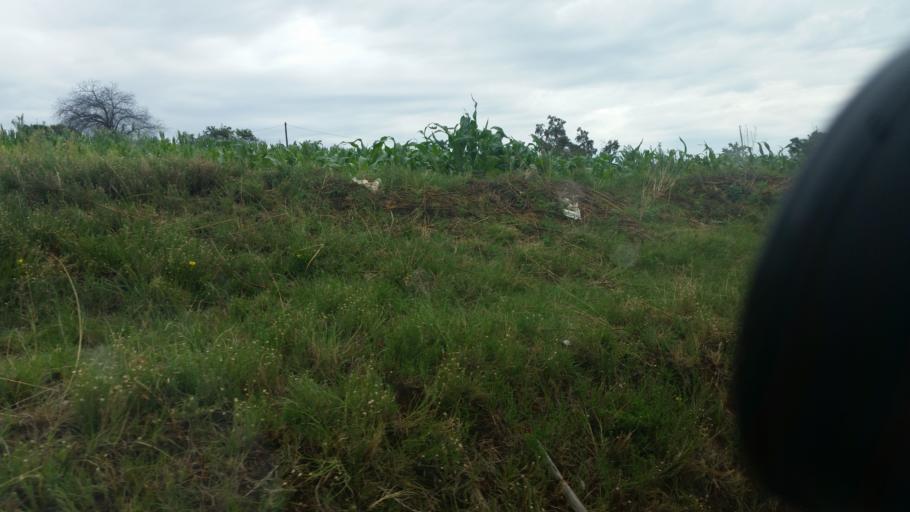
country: LS
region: Berea
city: Teyateyaneng
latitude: -29.1069
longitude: 27.9658
